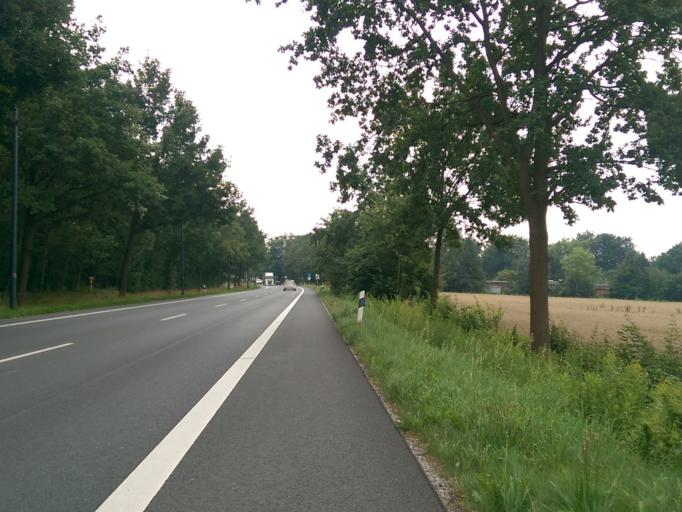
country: DE
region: North Rhine-Westphalia
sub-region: Regierungsbezirk Detmold
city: Guetersloh
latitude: 51.9228
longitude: 8.3660
